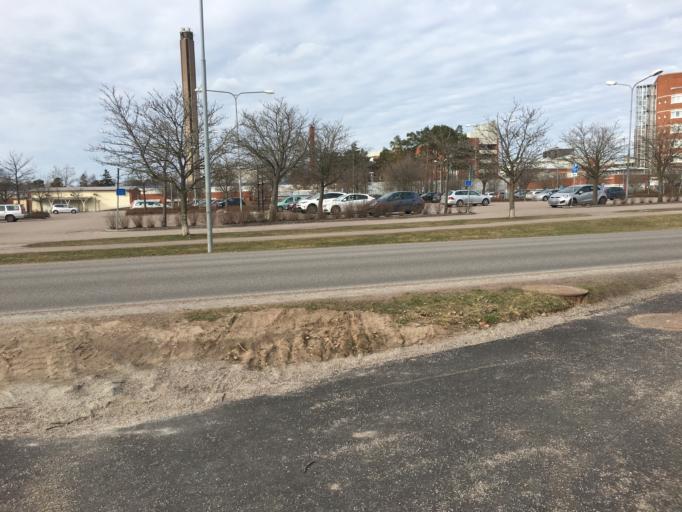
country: SE
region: Kalmar
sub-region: Kalmar Kommun
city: Kalmar
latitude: 56.6565
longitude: 16.3279
